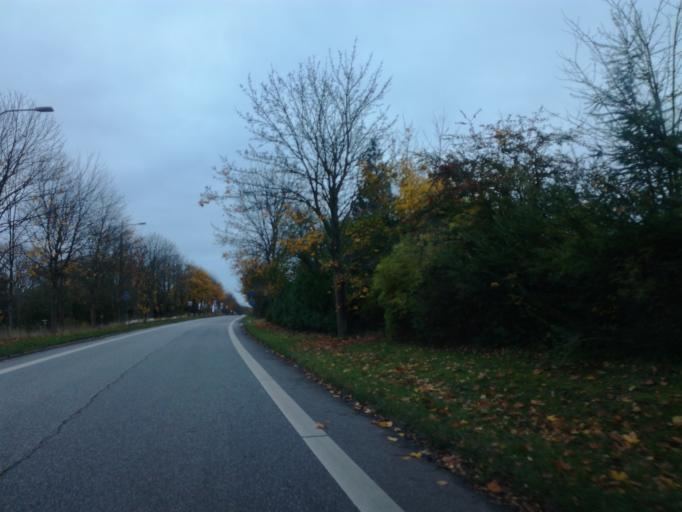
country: DK
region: South Denmark
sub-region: Fredericia Kommune
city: Snoghoj
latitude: 55.5505
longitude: 9.6941
